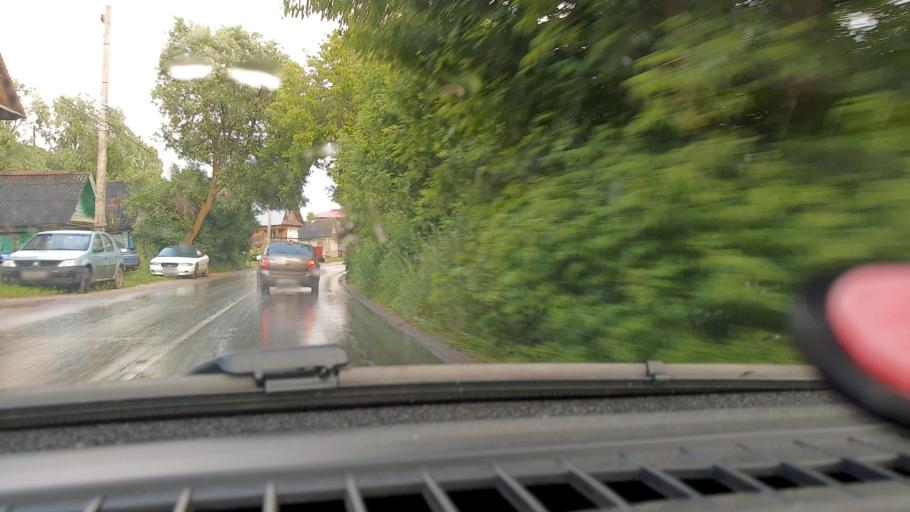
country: RU
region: Nizjnij Novgorod
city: Gorodets
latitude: 56.6636
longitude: 43.4577
